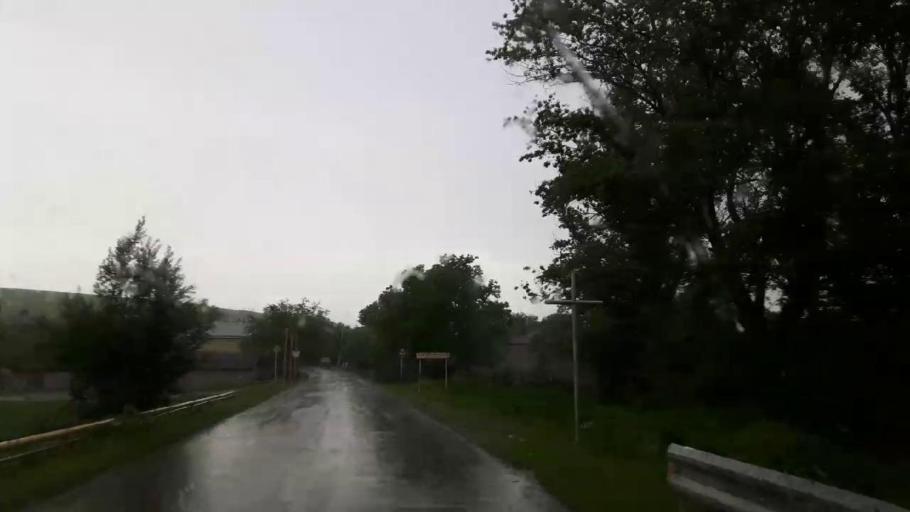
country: GE
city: Agara
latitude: 42.0128
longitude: 43.8524
